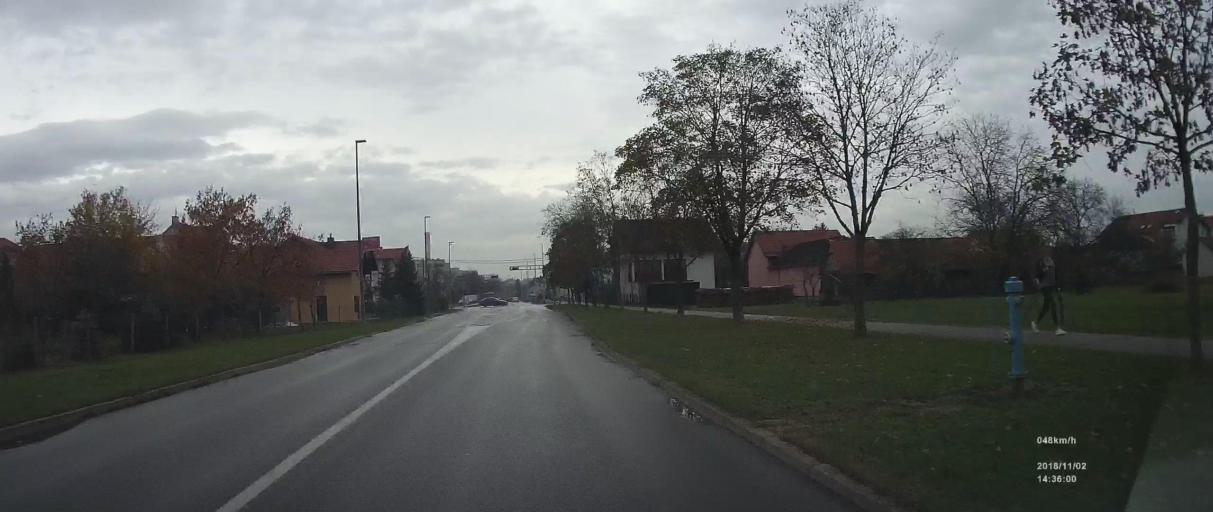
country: HR
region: Zagrebacka
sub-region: Grad Velika Gorica
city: Velika Gorica
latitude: 45.7071
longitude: 16.0652
